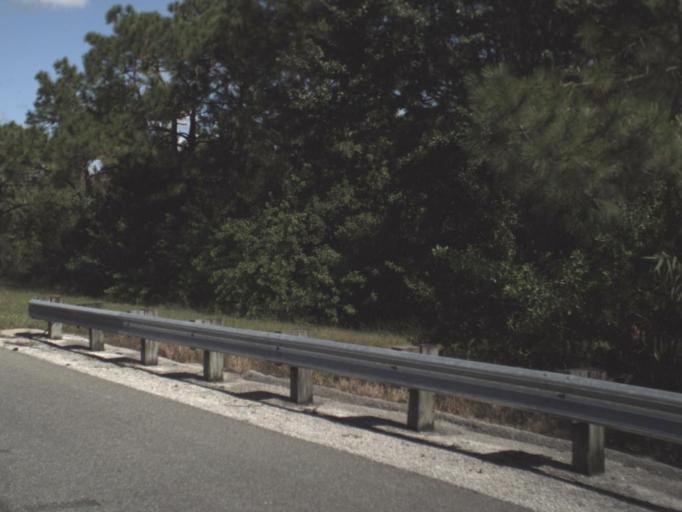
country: US
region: Florida
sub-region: Osceola County
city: Saint Cloud
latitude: 28.1527
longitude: -81.2976
